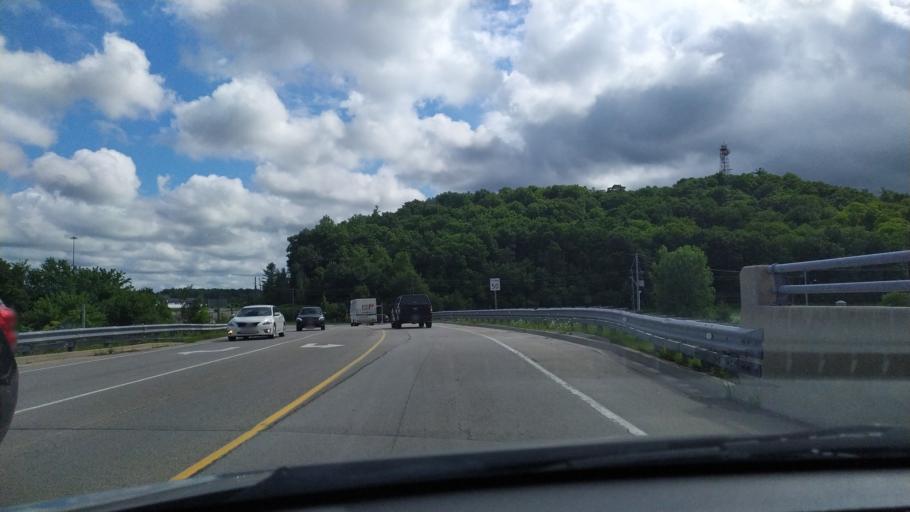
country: CA
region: Ontario
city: Cambridge
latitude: 43.3850
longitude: -80.4073
